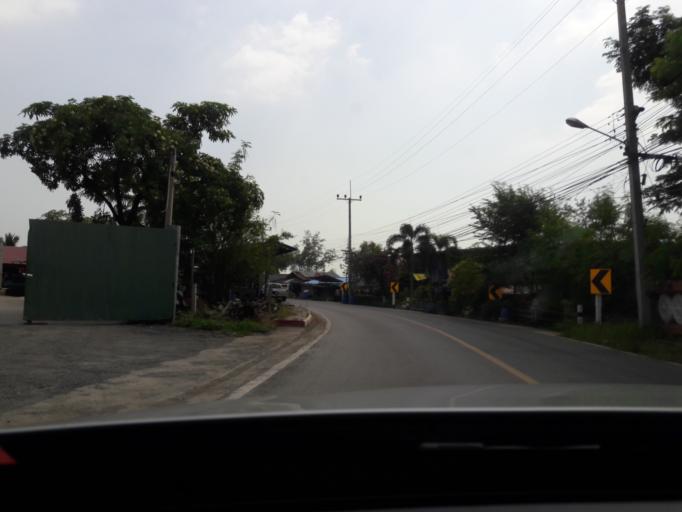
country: TH
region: Samut Songkhram
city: Amphawa
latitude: 13.3517
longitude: 99.9355
